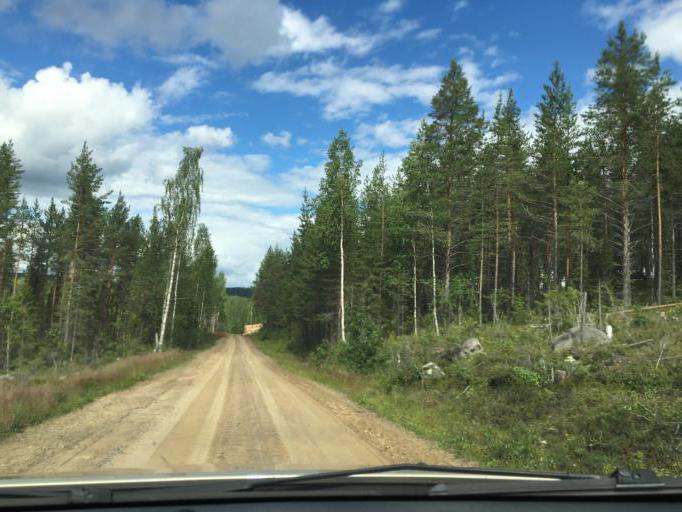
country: SE
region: Norrbotten
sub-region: Overkalix Kommun
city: OEverkalix
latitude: 66.1490
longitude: 22.7973
